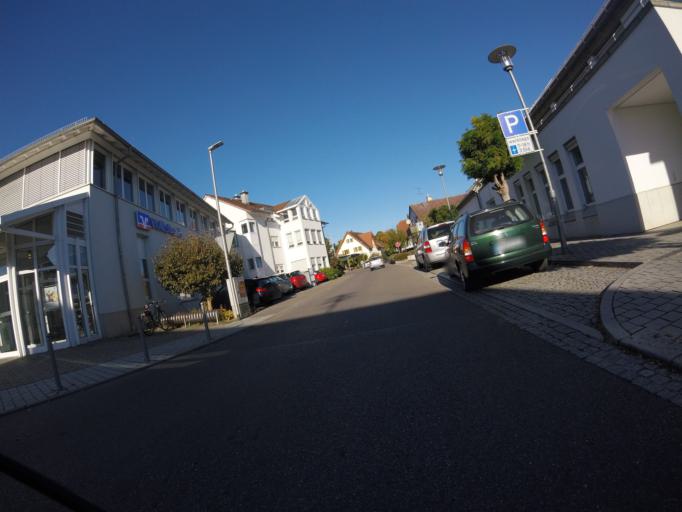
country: DE
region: Baden-Wuerttemberg
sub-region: Regierungsbezirk Stuttgart
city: Murr
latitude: 48.9618
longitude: 9.2585
